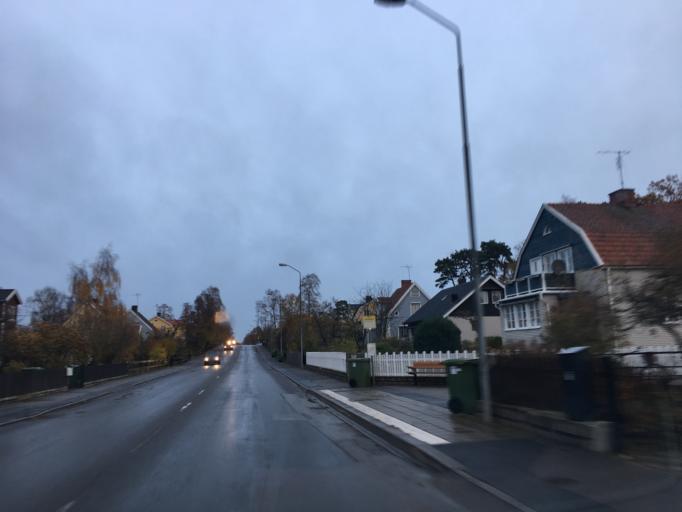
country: SE
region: Kalmar
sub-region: Kalmar Kommun
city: Kalmar
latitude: 56.6888
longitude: 16.3557
